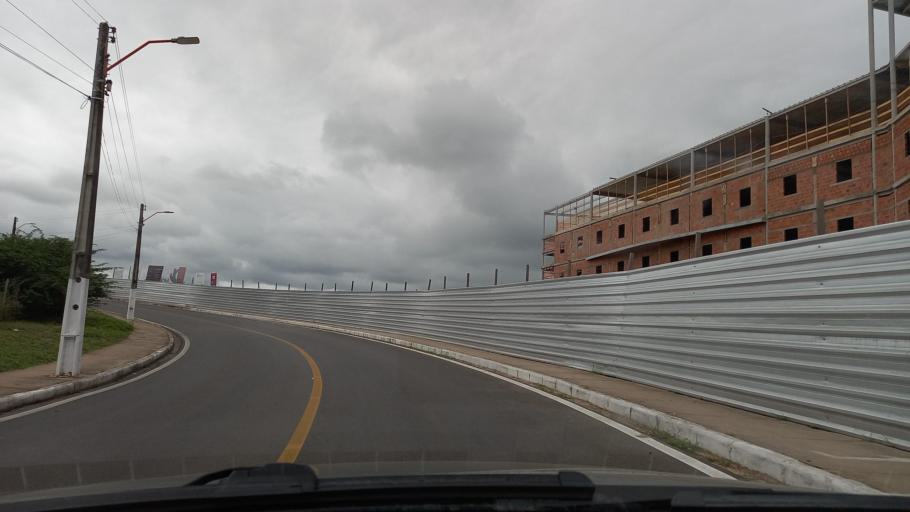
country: BR
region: Sergipe
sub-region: Caninde De Sao Francisco
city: Caninde de Sao Francisco
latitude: -9.6155
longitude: -37.7637
